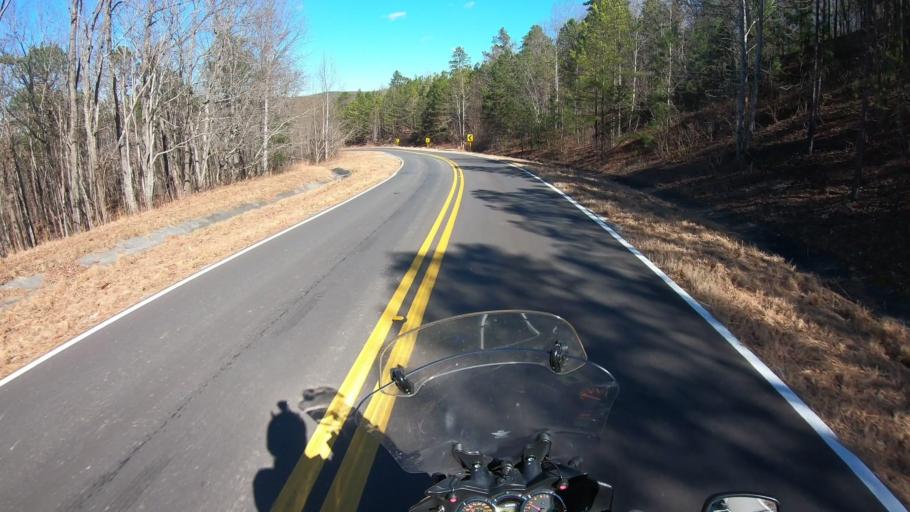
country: US
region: Alabama
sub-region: Talladega County
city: Munford
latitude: 33.4151
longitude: -85.8736
